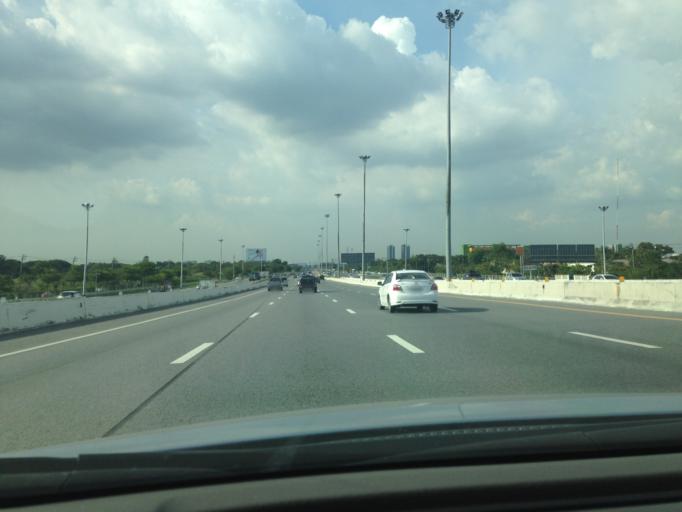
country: TH
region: Bangkok
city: Bueng Kum
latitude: 13.7934
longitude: 100.6824
